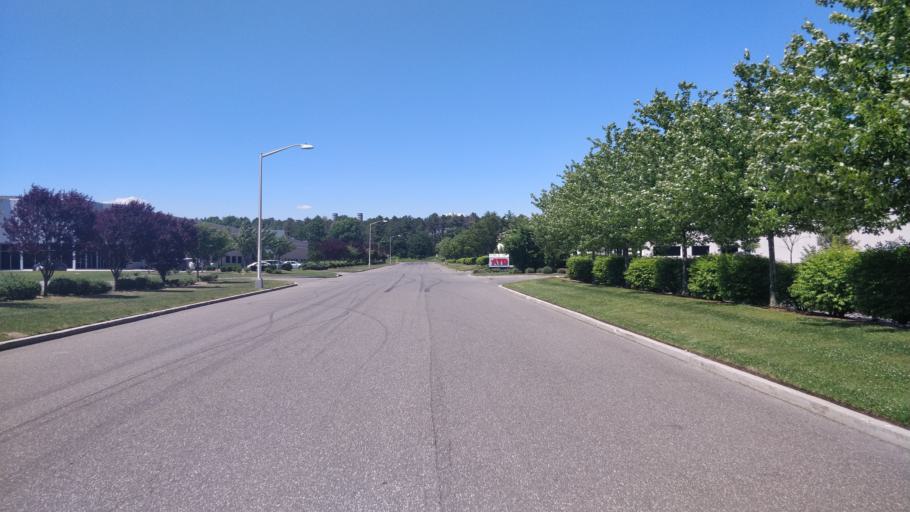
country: US
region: New York
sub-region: Suffolk County
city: Bay Wood
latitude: 40.7817
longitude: -73.2921
